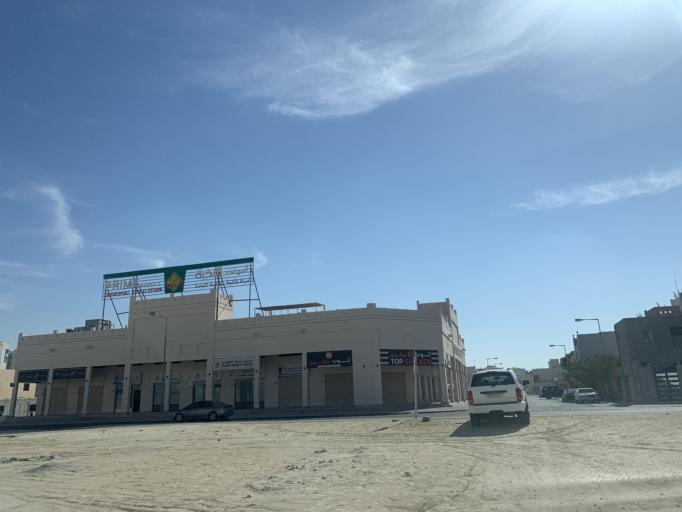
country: BH
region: Central Governorate
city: Madinat Hamad
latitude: 26.1152
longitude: 50.4877
